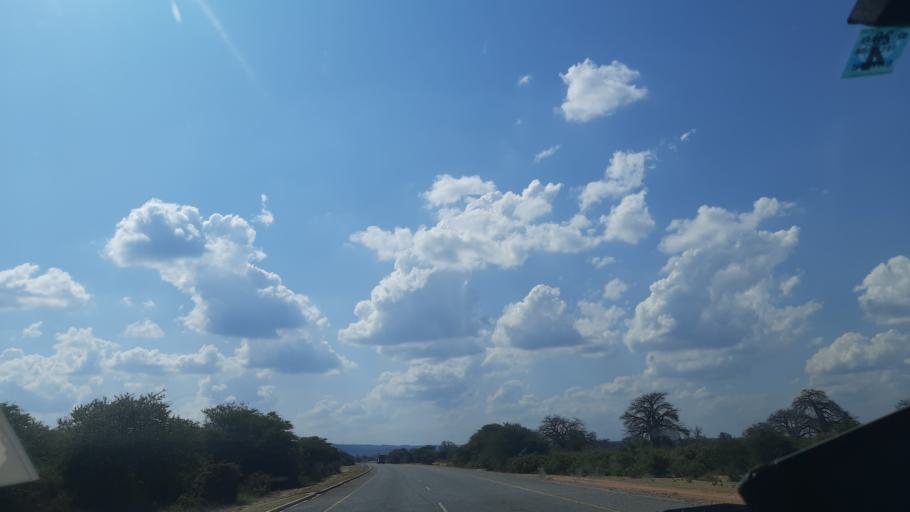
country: TZ
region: Singida
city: Kilimatinde
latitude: -5.8378
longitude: 35.0644
